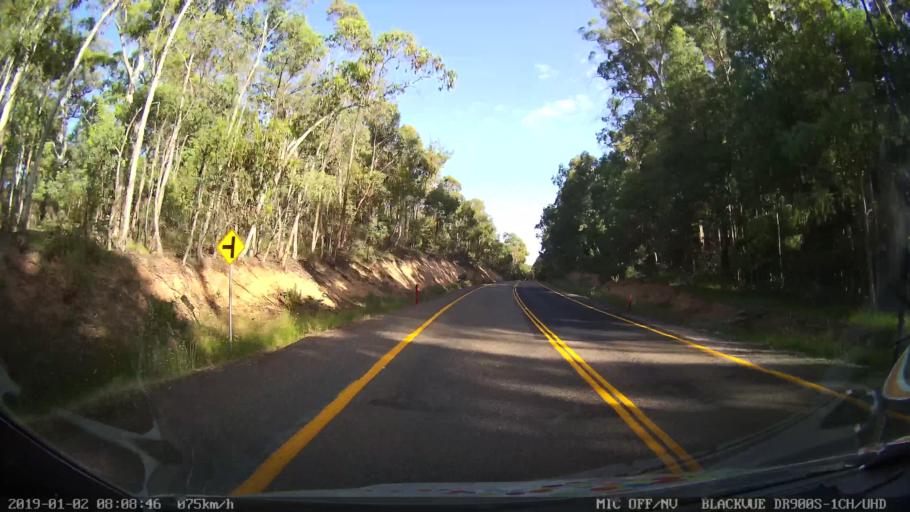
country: AU
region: New South Wales
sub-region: Tumut Shire
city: Tumut
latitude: -35.6137
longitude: 148.3825
